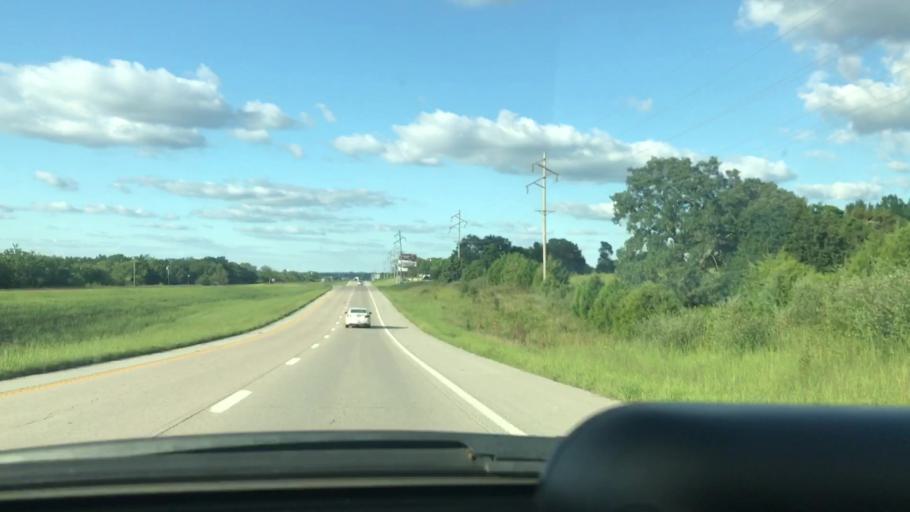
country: US
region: Missouri
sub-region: Pettis County
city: Sedalia
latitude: 38.6380
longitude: -93.2658
